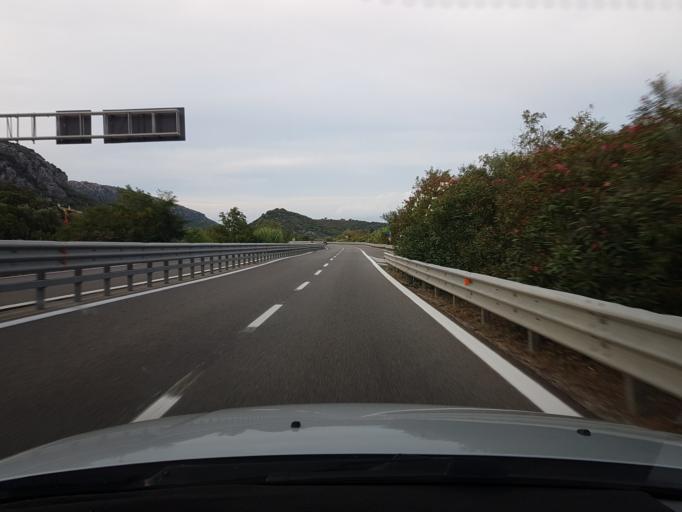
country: IT
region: Sardinia
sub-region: Provincia di Nuoro
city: Siniscola
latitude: 40.5875
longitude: 9.6921
